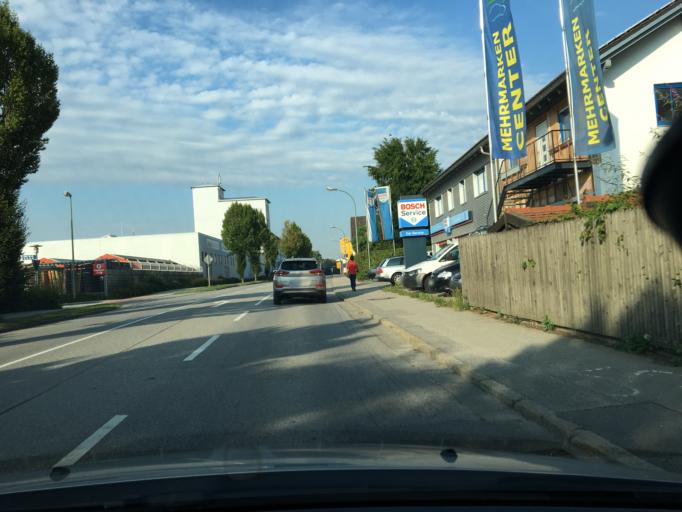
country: DE
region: Bavaria
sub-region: Lower Bavaria
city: Vilsbiburg
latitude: 48.4530
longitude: 12.3605
